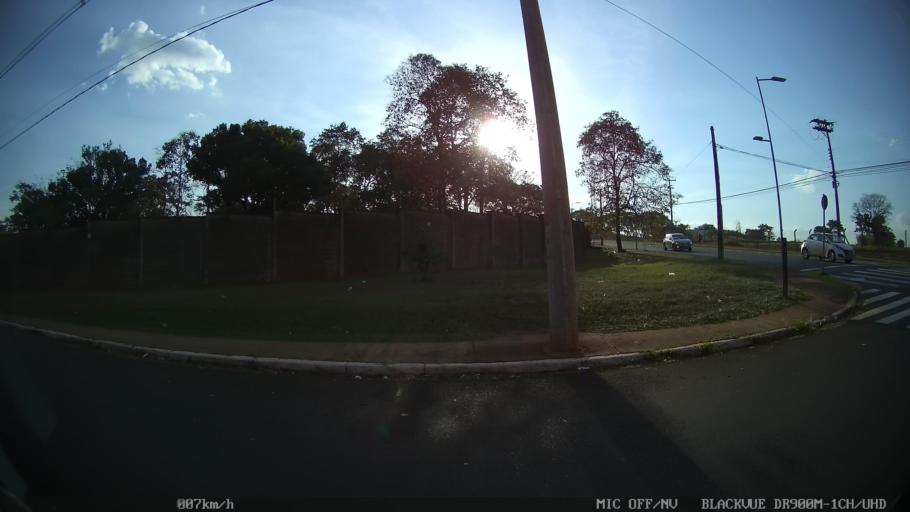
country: BR
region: Sao Paulo
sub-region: Ribeirao Preto
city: Ribeirao Preto
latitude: -21.1644
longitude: -47.8444
